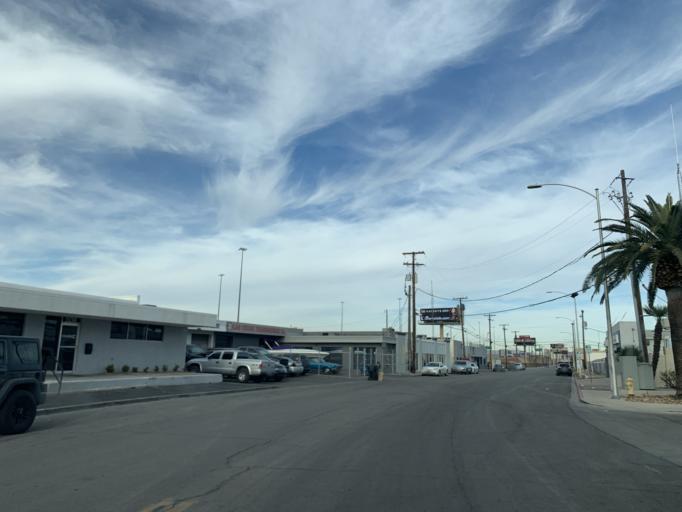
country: US
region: Nevada
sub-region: Clark County
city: Las Vegas
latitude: 36.1473
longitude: -115.1671
